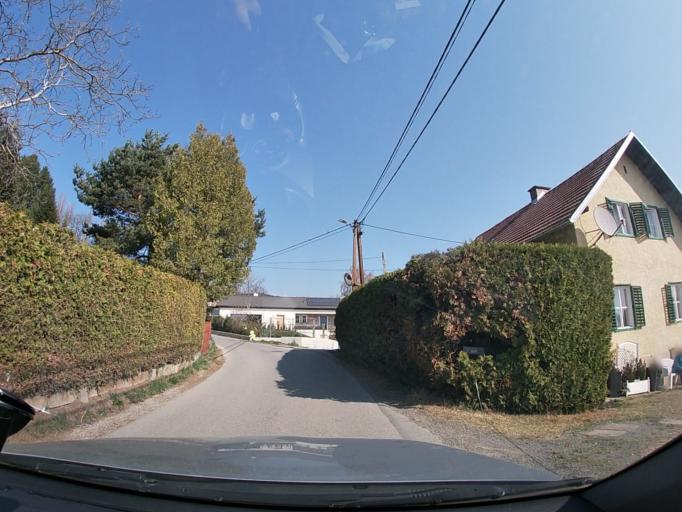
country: AT
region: Styria
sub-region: Politischer Bezirk Graz-Umgebung
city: Raaba
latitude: 47.0450
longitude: 15.4916
